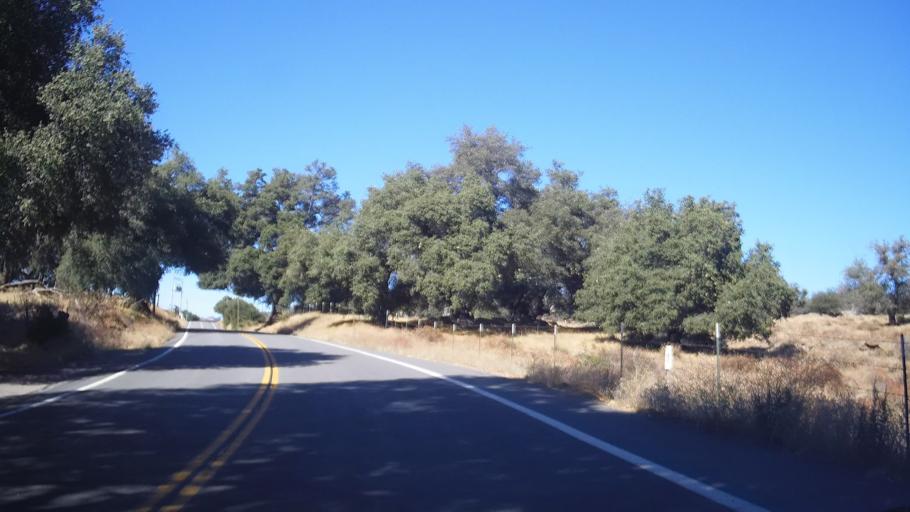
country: US
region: California
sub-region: San Diego County
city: Julian
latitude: 33.0608
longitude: -116.6179
